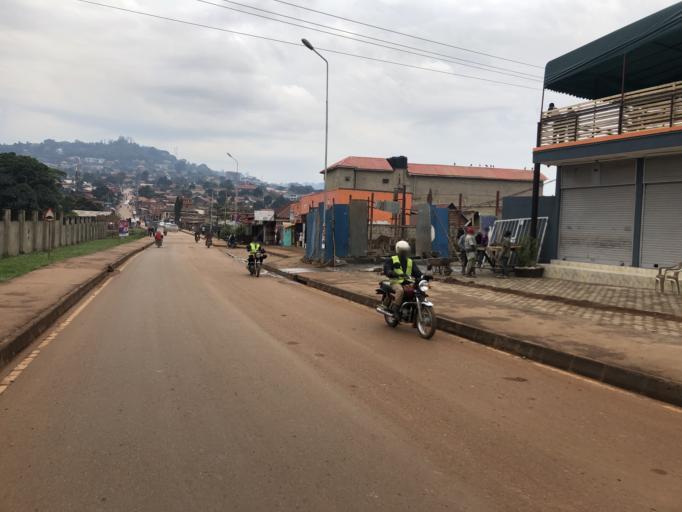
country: UG
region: Central Region
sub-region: Kampala District
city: Kampala
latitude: 0.2842
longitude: 32.6050
